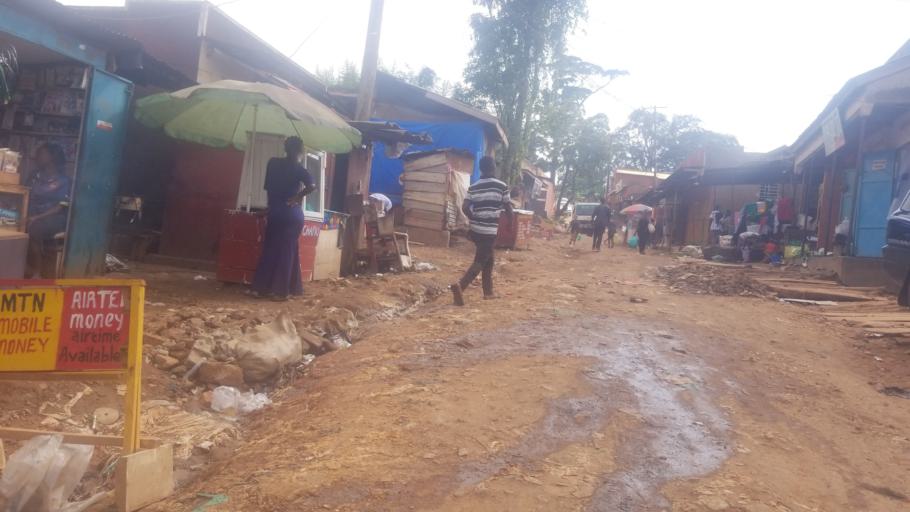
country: UG
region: Central Region
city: Kampala Central Division
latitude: 0.3305
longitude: 32.5586
